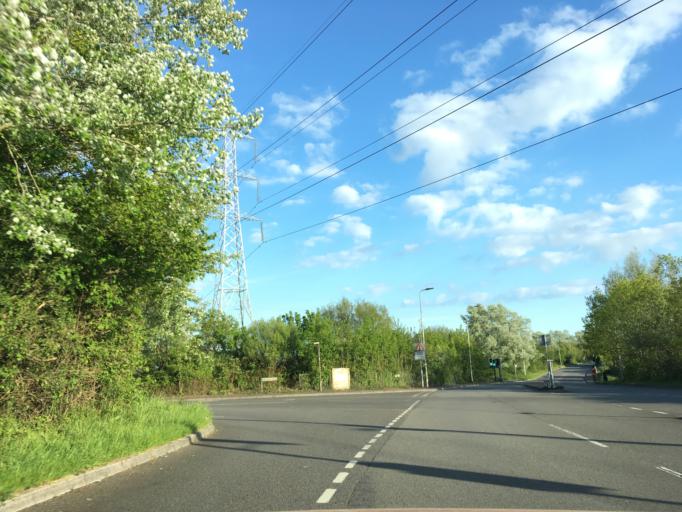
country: GB
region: Wales
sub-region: Newport
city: Marshfield
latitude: 51.5281
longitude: -3.0883
